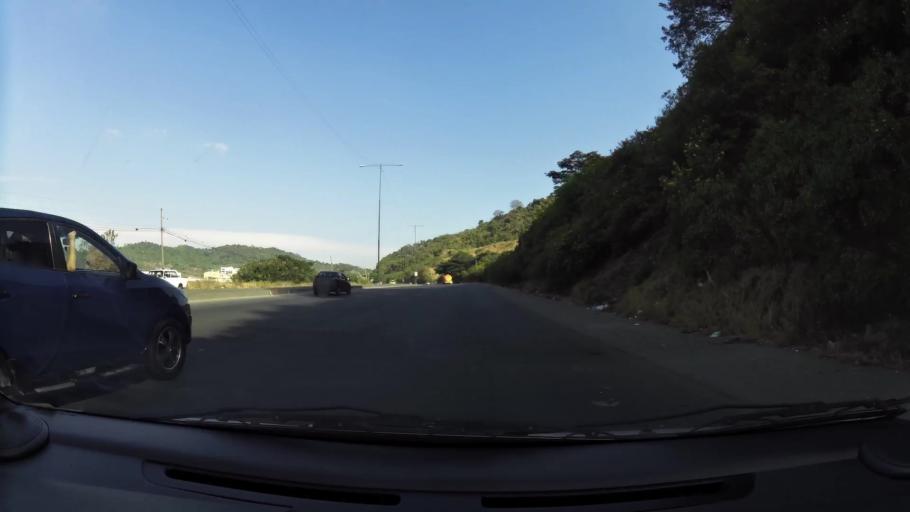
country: EC
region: Guayas
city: Santa Lucia
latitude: -2.1643
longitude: -79.9484
